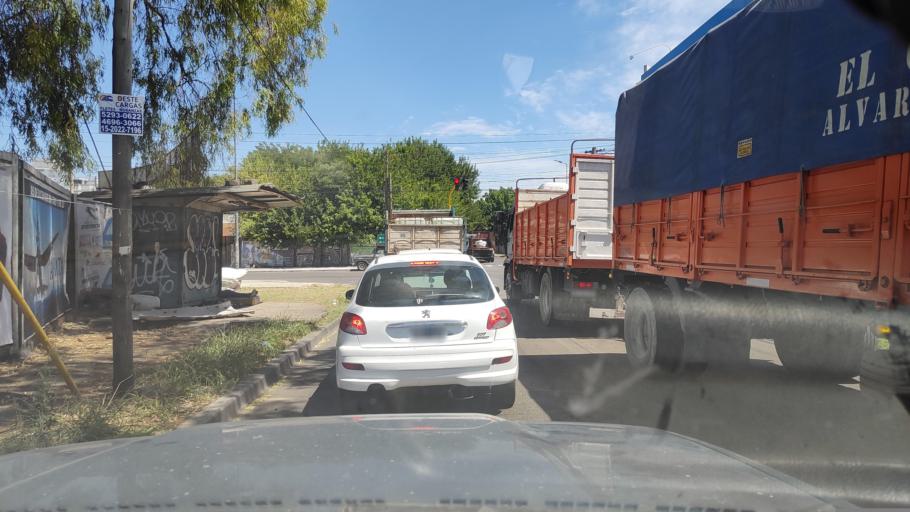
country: AR
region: Buenos Aires
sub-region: Partido de Moron
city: Moron
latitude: -34.6599
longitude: -58.6064
